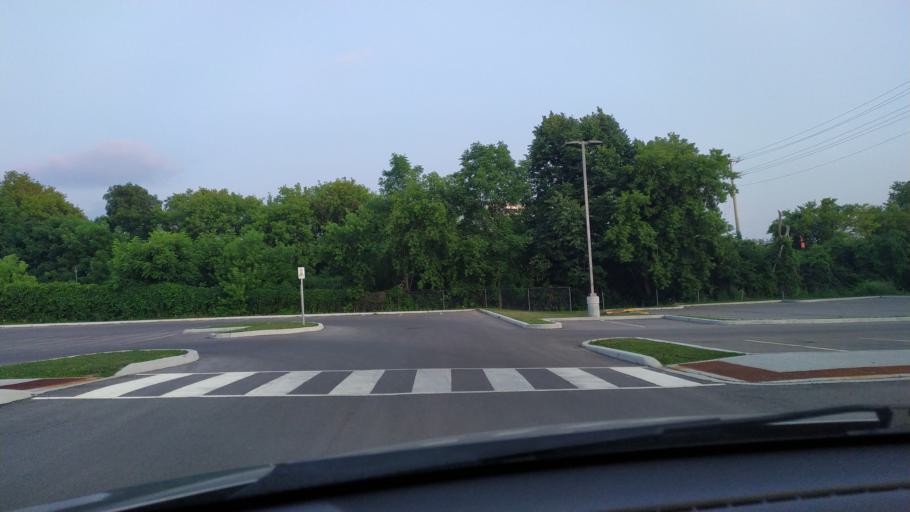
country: CA
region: Ontario
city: Waterloo
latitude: 43.4496
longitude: -80.5137
